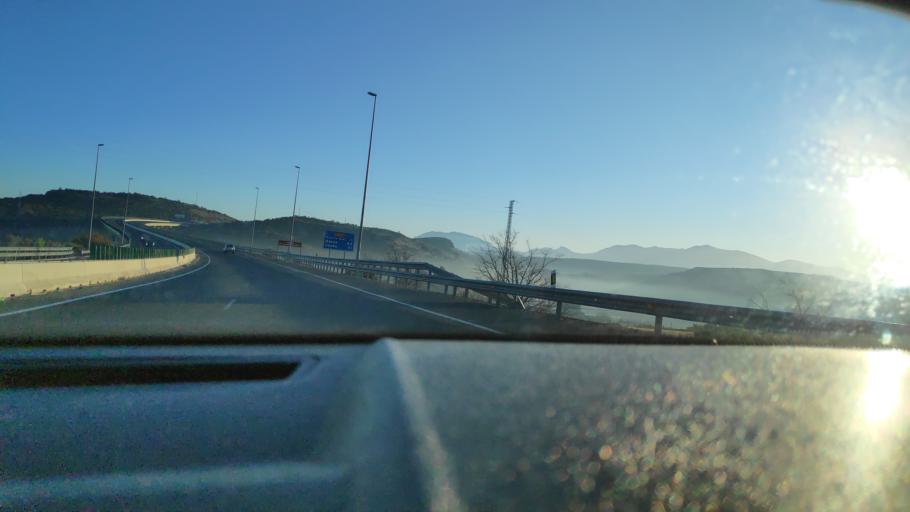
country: ES
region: Andalusia
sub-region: Provincia de Jaen
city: Jaen
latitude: 37.8189
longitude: -3.7604
